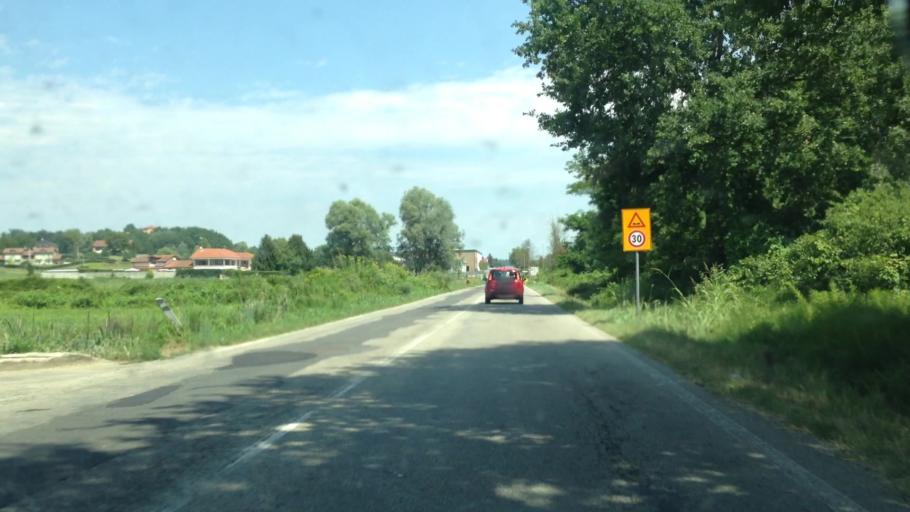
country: IT
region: Piedmont
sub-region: Provincia di Asti
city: Asti
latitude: 44.9325
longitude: 8.2252
